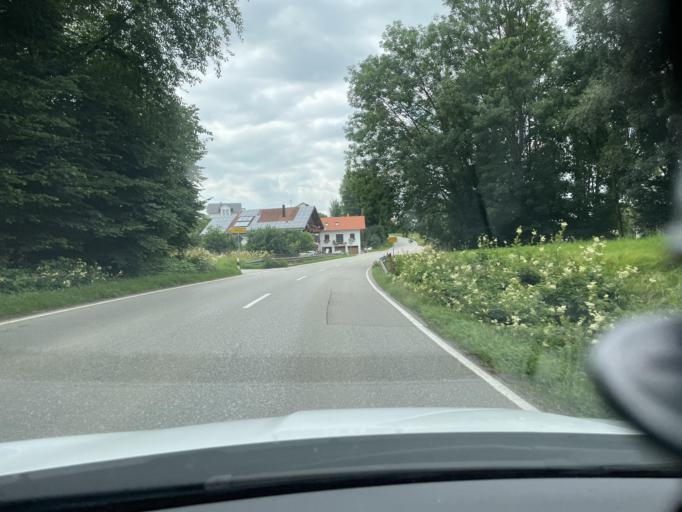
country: DE
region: Bavaria
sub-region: Upper Bavaria
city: Sankt Wolfgang
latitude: 48.2076
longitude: 12.1380
